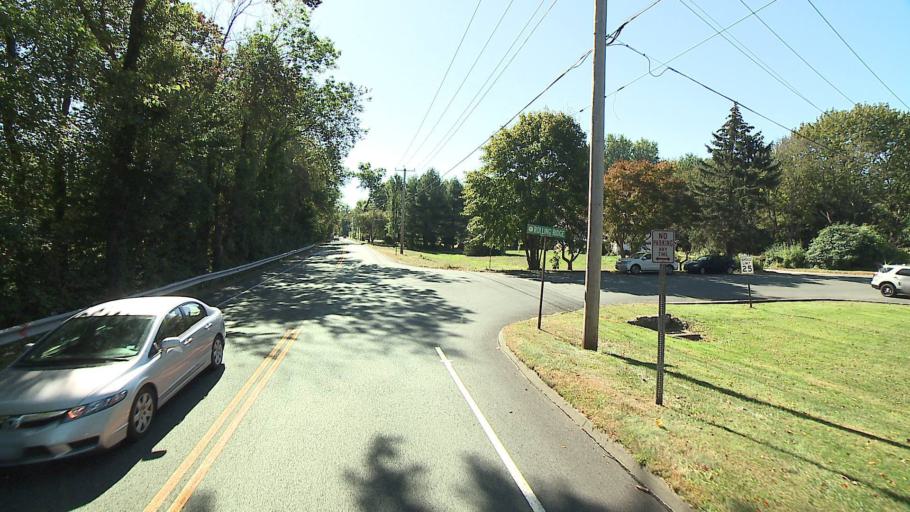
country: US
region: Connecticut
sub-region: New Haven County
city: Orange
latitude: 41.2774
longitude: -73.0071
